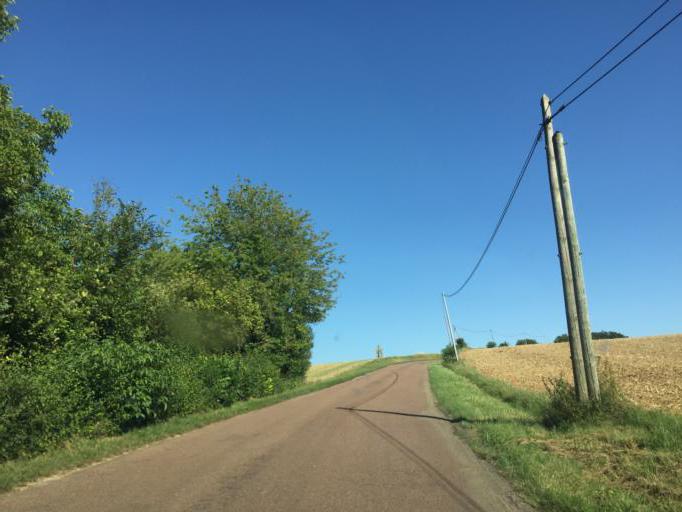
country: FR
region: Bourgogne
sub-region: Departement de l'Yonne
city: Fontenailles
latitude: 47.5019
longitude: 3.3593
